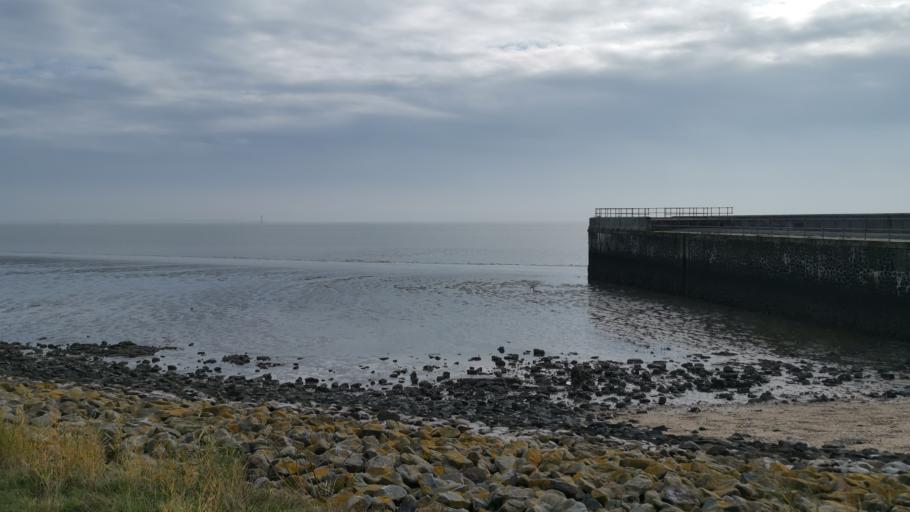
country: DE
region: Lower Saxony
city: Wilhelmshaven
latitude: 53.5185
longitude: 8.1594
